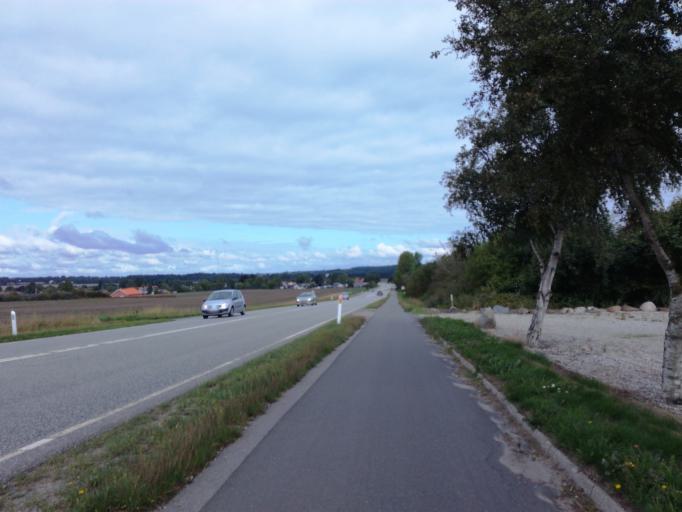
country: DK
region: South Denmark
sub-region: Vejle Kommune
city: Borkop
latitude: 55.6344
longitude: 9.6064
